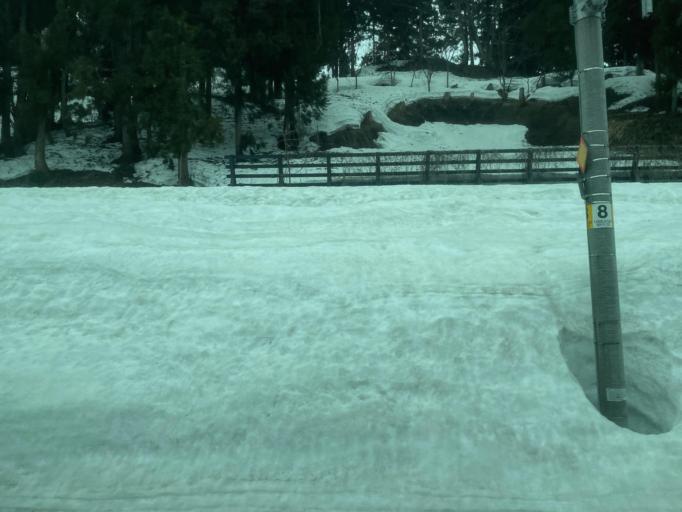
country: JP
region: Niigata
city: Shiozawa
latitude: 37.0270
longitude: 138.8246
